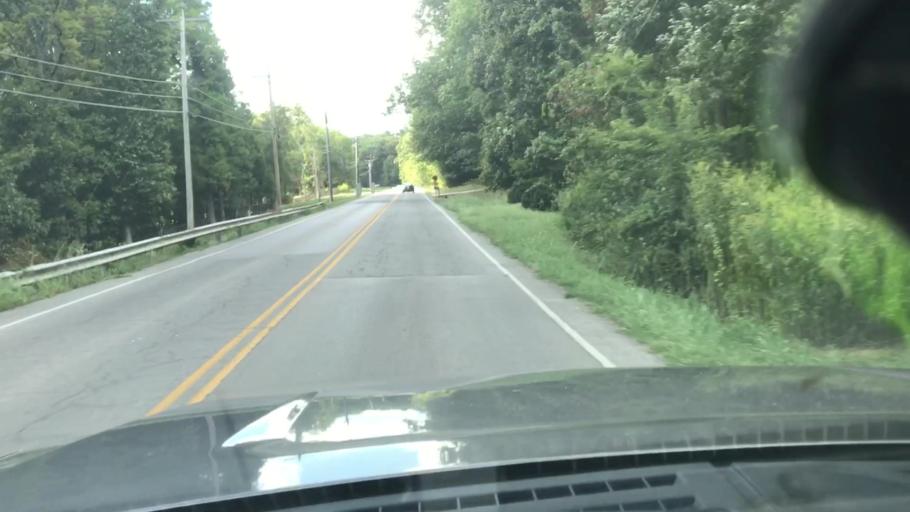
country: US
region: Tennessee
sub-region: Davidson County
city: Forest Hills
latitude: 36.0223
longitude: -86.8891
